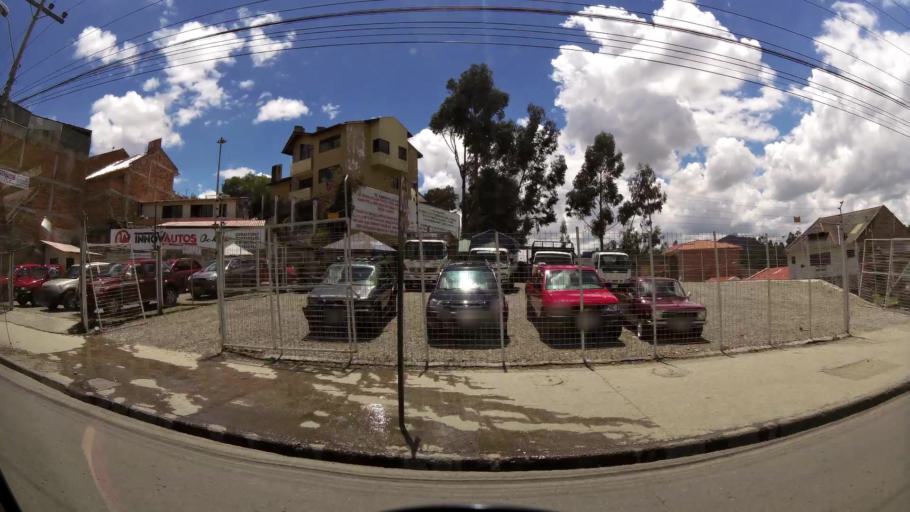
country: EC
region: Azuay
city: Cuenca
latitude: -2.9037
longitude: -79.0314
